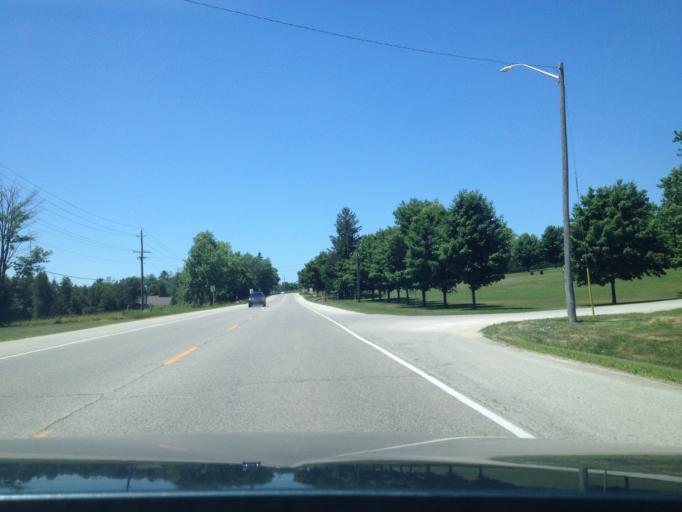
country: CA
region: Ontario
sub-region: Wellington County
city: Guelph
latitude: 43.6914
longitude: -80.3983
